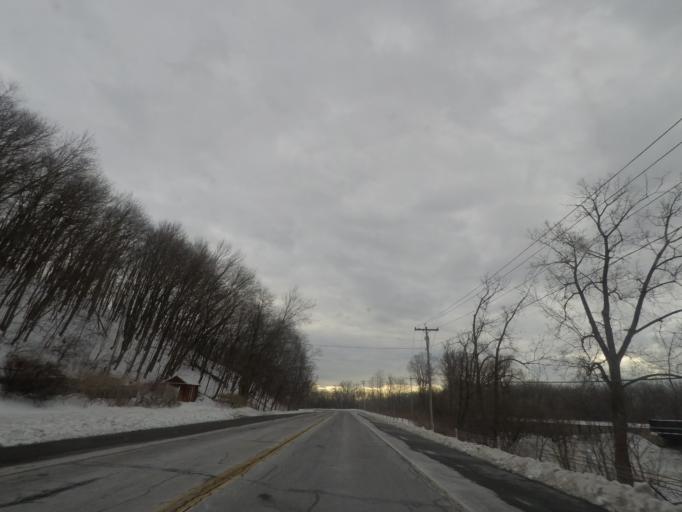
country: US
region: New York
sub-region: Rensselaer County
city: Castleton-on-Hudson
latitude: 42.5524
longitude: -73.7465
